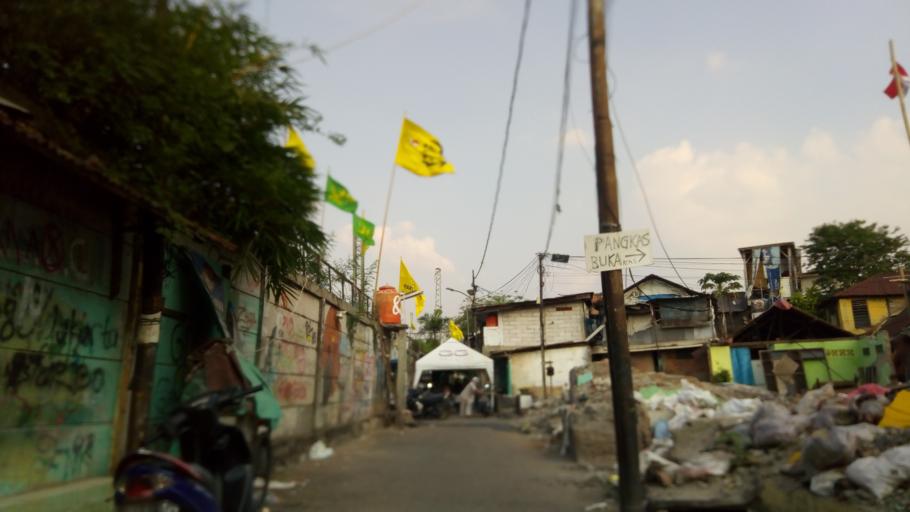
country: ID
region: Jakarta Raya
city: Jakarta
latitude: -6.2070
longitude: 106.8468
